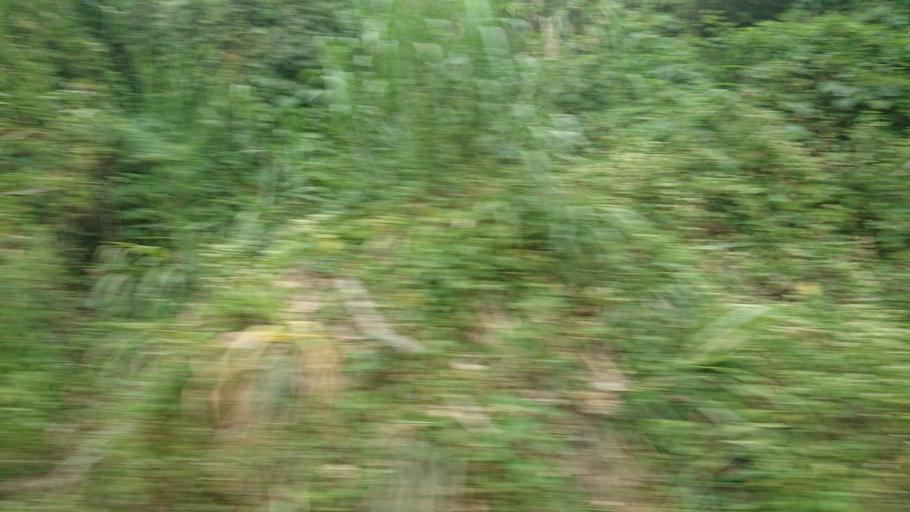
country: TW
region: Taiwan
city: Lugu
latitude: 23.6003
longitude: 120.6988
